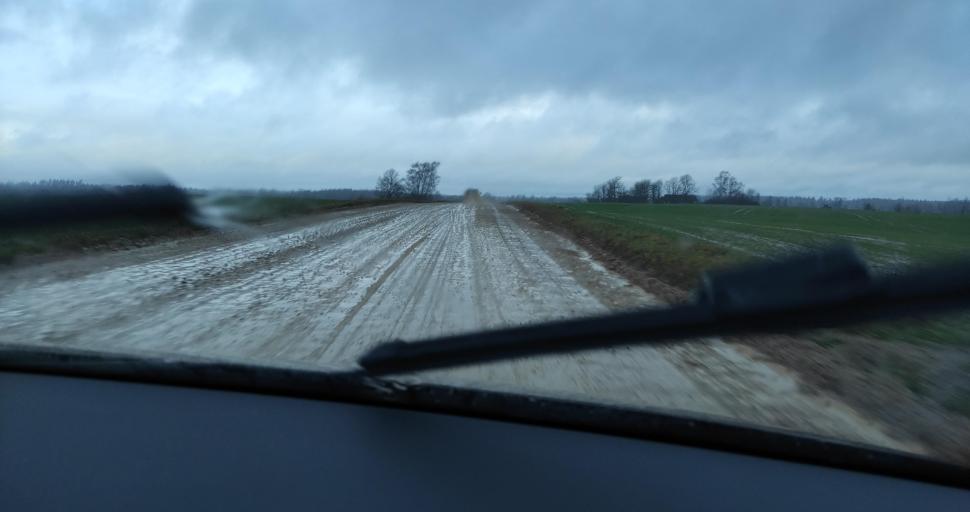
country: LV
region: Skrunda
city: Skrunda
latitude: 56.6966
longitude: 22.2144
